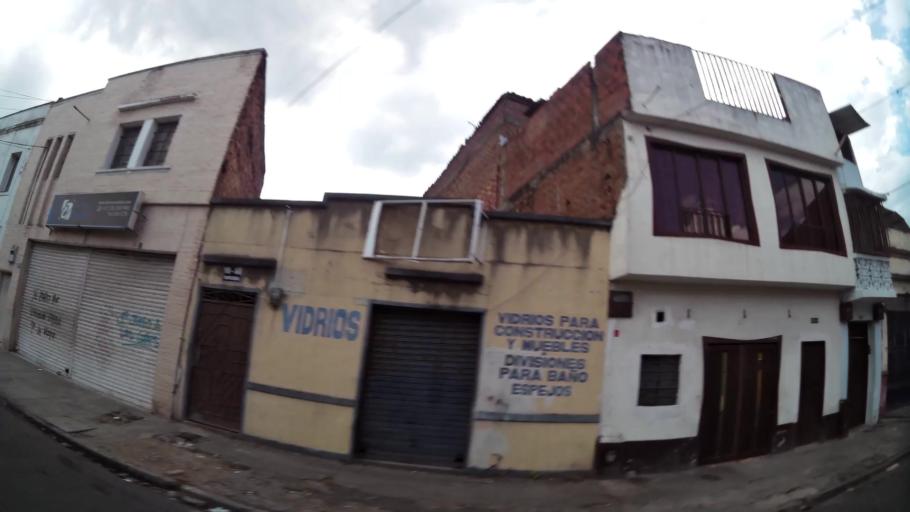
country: CO
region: Valle del Cauca
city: Cali
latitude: 3.4393
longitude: -76.5334
